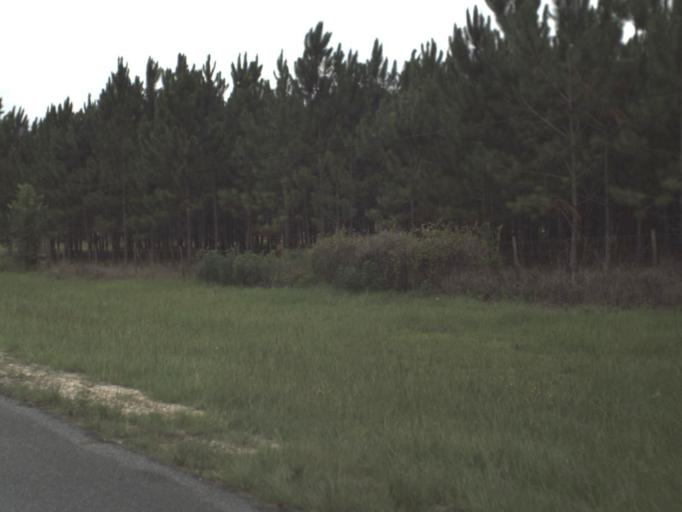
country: US
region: Florida
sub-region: Alachua County
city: Newberry
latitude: 29.6630
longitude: -82.6070
